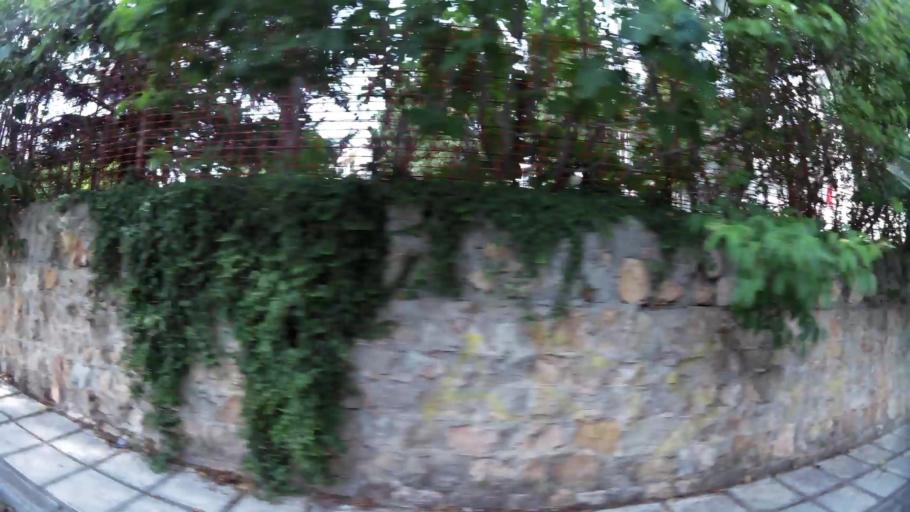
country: GR
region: Central Macedonia
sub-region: Nomos Thessalonikis
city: Oraiokastro
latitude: 40.7326
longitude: 22.9202
